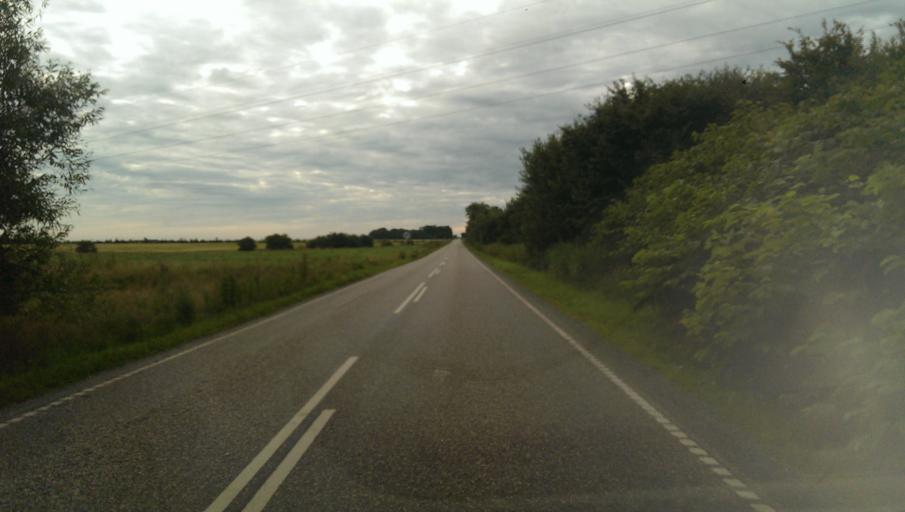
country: DK
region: South Denmark
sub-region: Esbjerg Kommune
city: Tjaereborg
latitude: 55.5183
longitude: 8.5182
